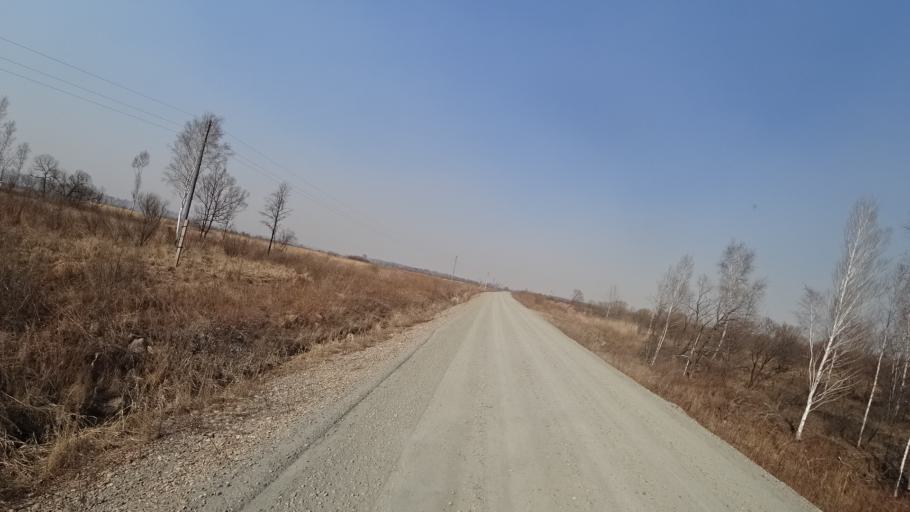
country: RU
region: Amur
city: Novobureyskiy
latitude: 49.8053
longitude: 129.9638
